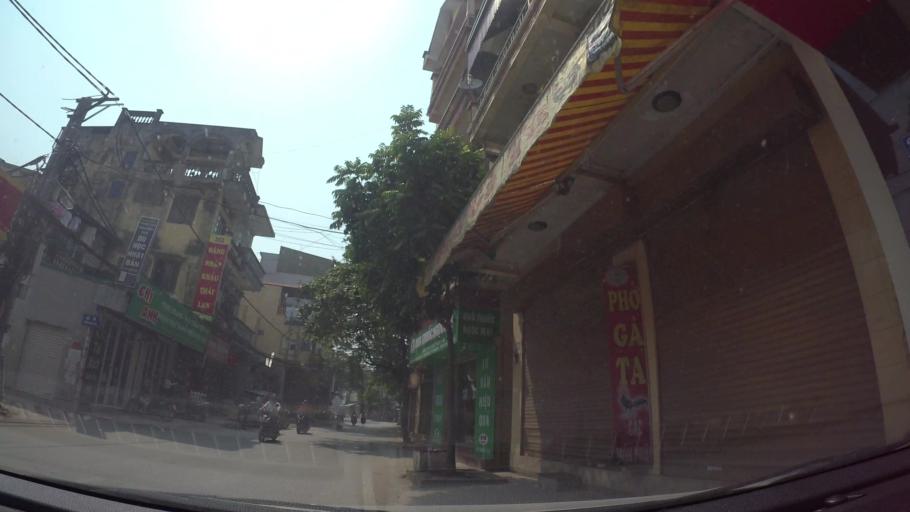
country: VN
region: Ha Noi
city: Ha Dong
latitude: 20.9953
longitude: 105.7583
